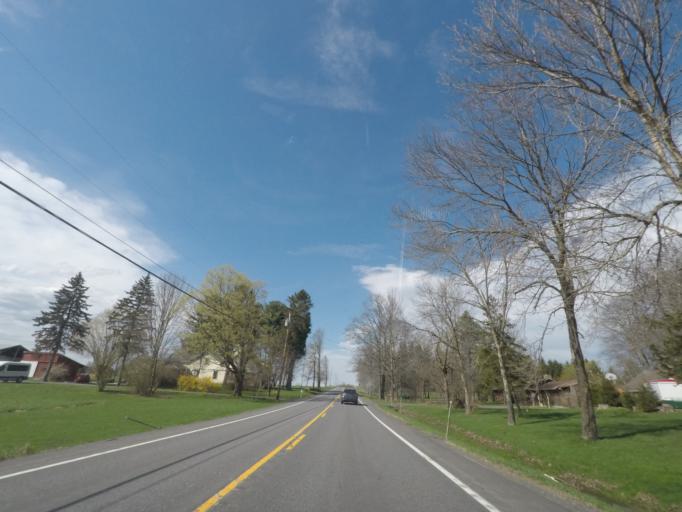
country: US
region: New York
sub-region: Greene County
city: Cairo
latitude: 42.4574
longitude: -74.0052
